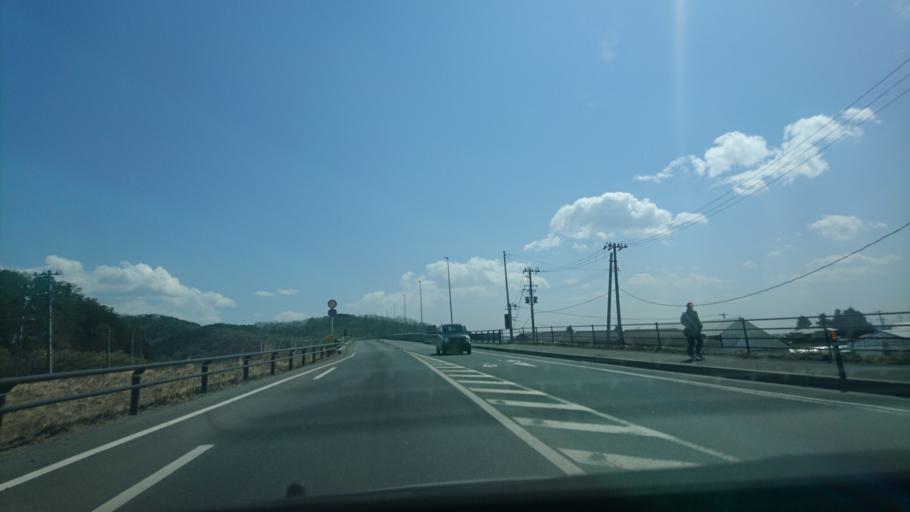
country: JP
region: Miyagi
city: Ishinomaki
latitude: 38.4596
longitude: 141.2847
